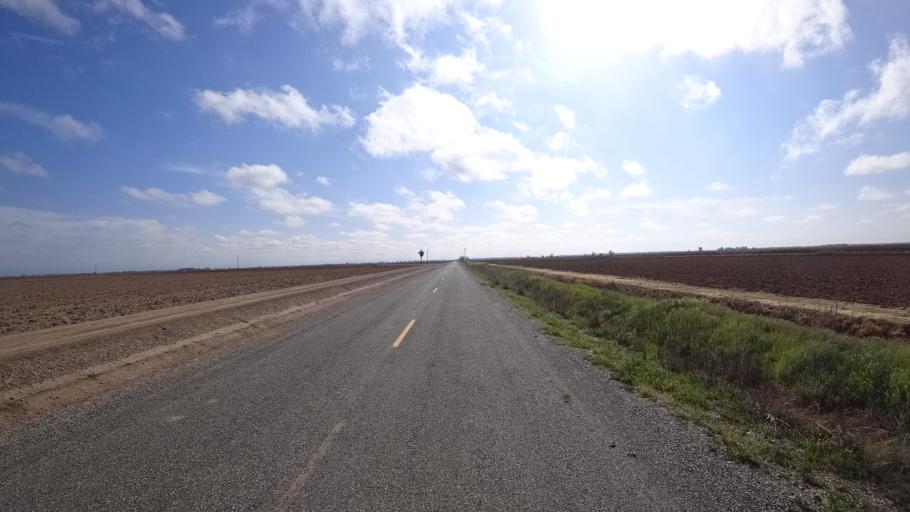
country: US
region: California
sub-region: Butte County
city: Durham
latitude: 39.5224
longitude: -121.9425
